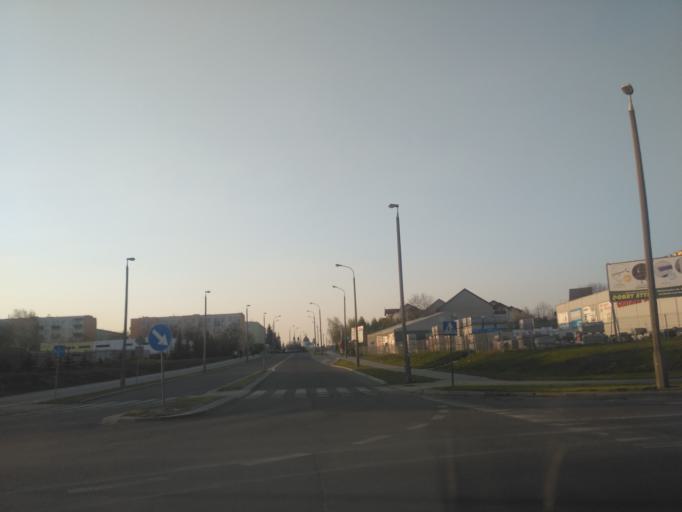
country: PL
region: Lublin Voivodeship
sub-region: Chelm
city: Chelm
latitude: 51.1212
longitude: 23.4838
